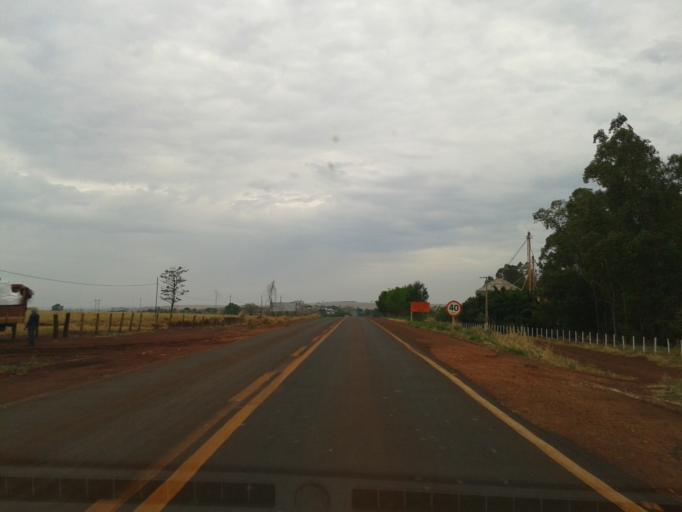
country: BR
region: Minas Gerais
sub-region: Capinopolis
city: Capinopolis
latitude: -18.7048
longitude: -49.5604
